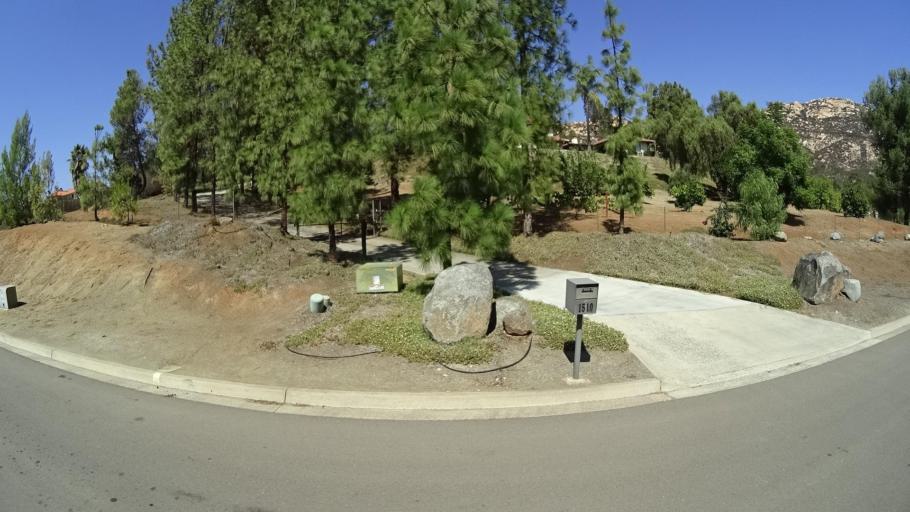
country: US
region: California
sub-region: San Diego County
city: Harbison Canyon
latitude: 32.8312
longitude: -116.8424
